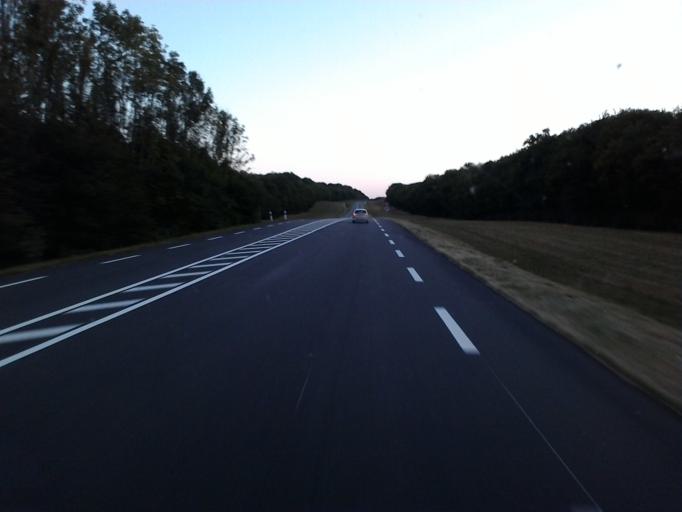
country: FR
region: Franche-Comte
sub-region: Departement du Jura
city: Poligny
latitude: 46.8369
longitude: 5.6154
